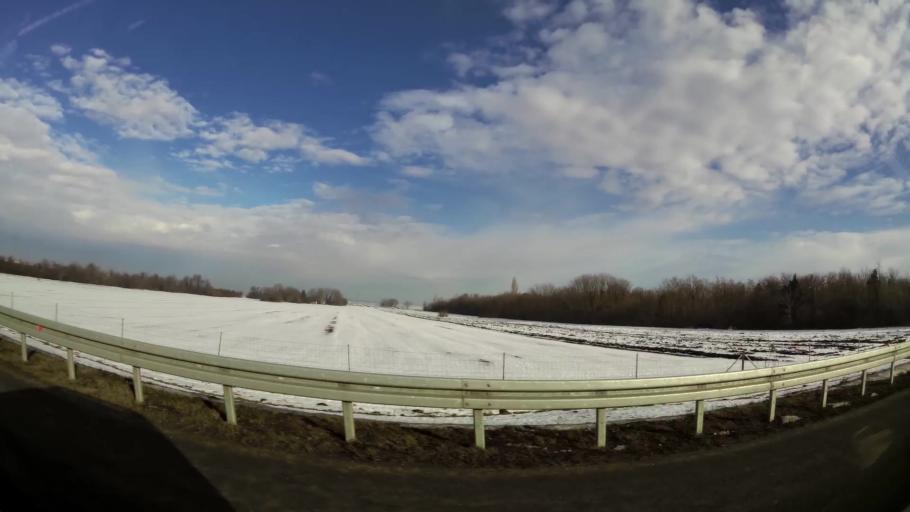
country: RS
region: Central Serbia
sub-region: Belgrade
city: Surcin
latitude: 44.8341
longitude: 20.3248
